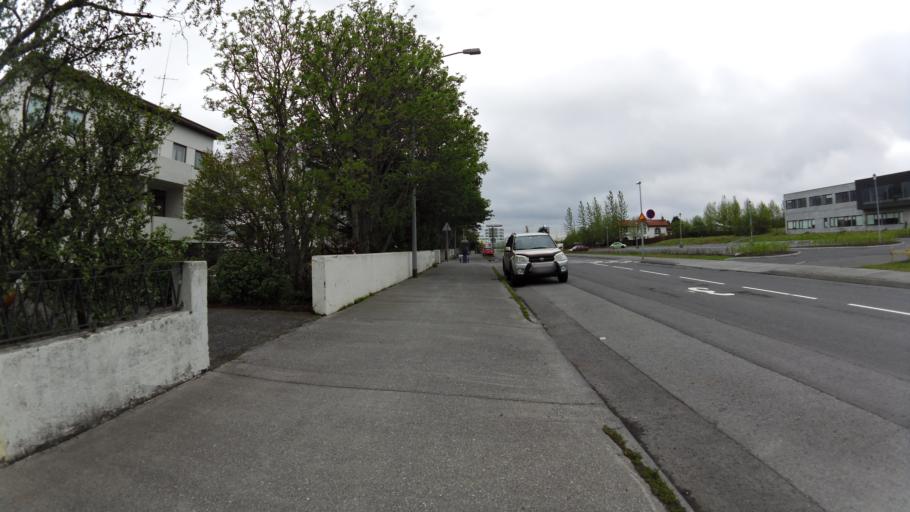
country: IS
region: Capital Region
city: Reykjavik
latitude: 64.1310
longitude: -21.9052
